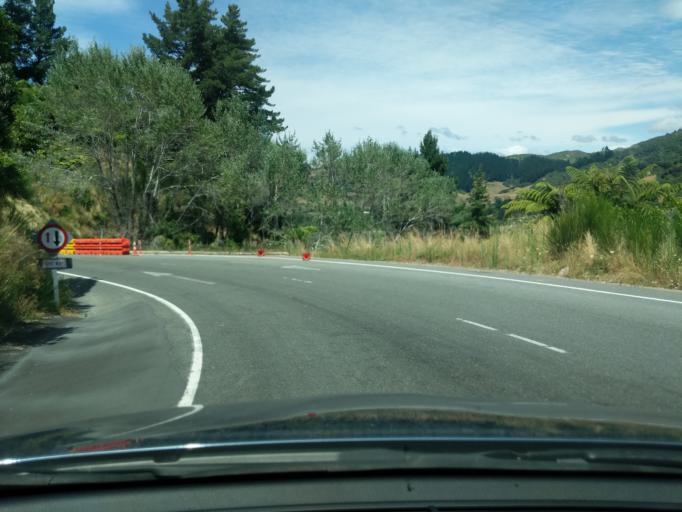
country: NZ
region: Tasman
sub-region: Tasman District
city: Motueka
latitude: -41.0515
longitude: 172.9619
